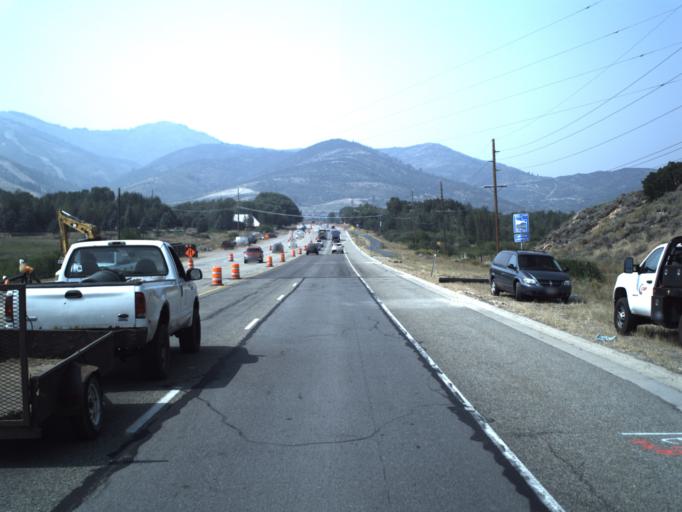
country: US
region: Utah
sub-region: Summit County
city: Snyderville
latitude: 40.6815
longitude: -111.5327
